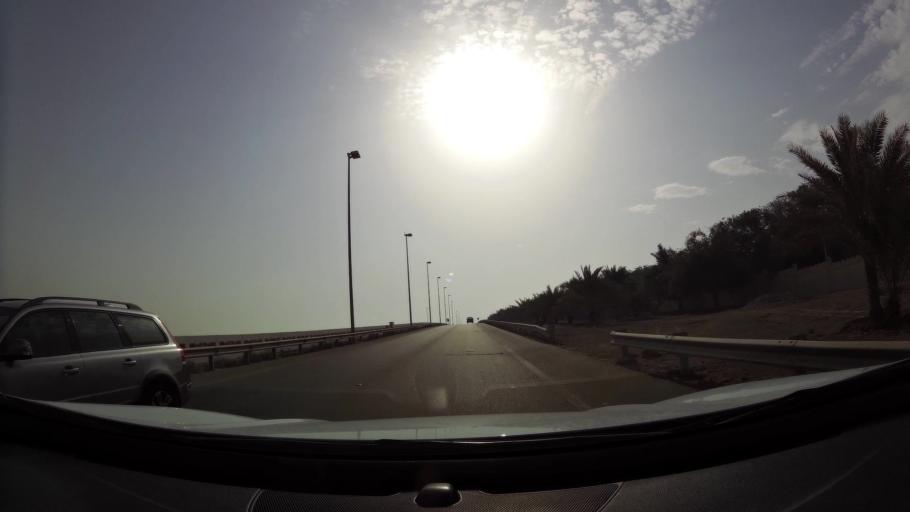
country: AE
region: Abu Dhabi
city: Abu Dhabi
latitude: 24.2461
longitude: 54.7088
